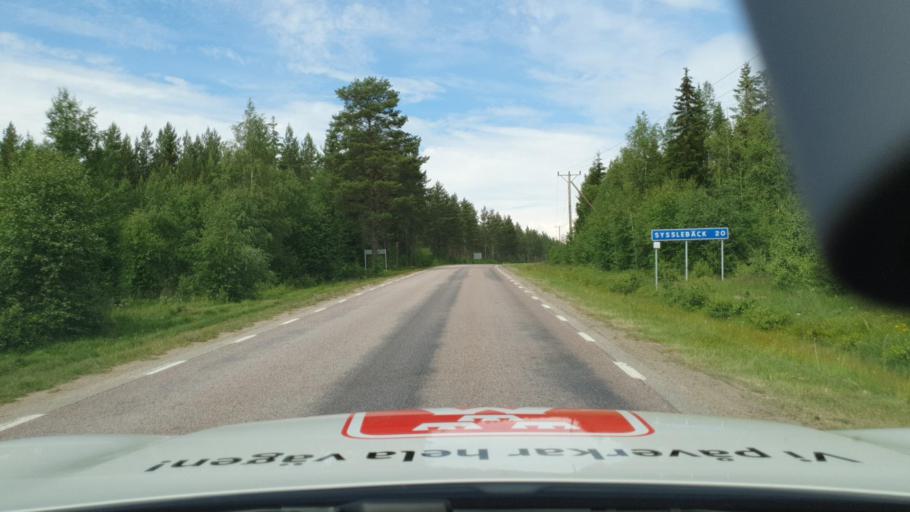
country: NO
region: Hedmark
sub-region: Grue
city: Kirkenaer
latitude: 60.7050
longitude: 12.6145
